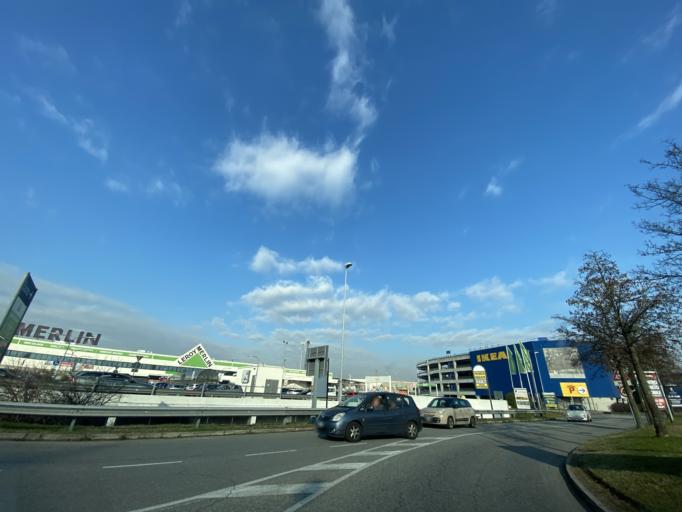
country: IT
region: Lombardy
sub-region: Citta metropolitana di Milano
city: Carugate
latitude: 45.5488
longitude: 9.3295
